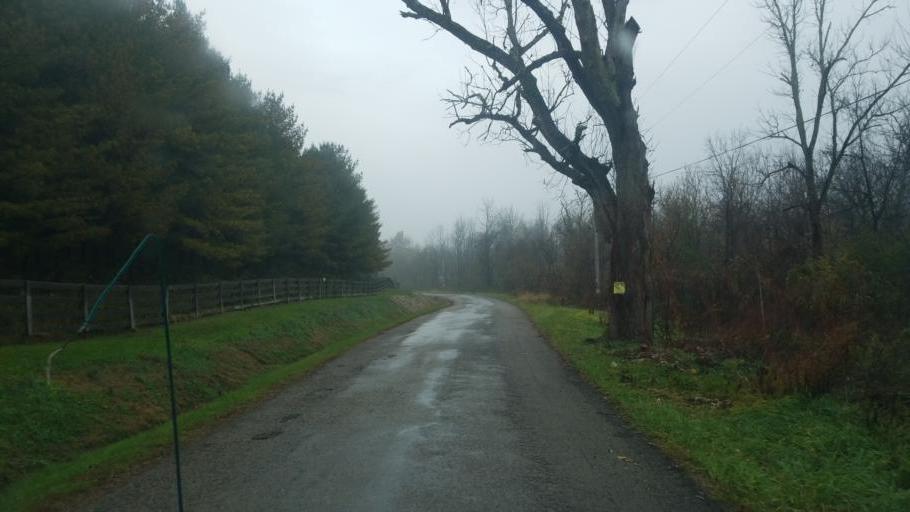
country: US
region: Ohio
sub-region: Athens County
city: Glouster
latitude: 39.4444
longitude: -81.9222
